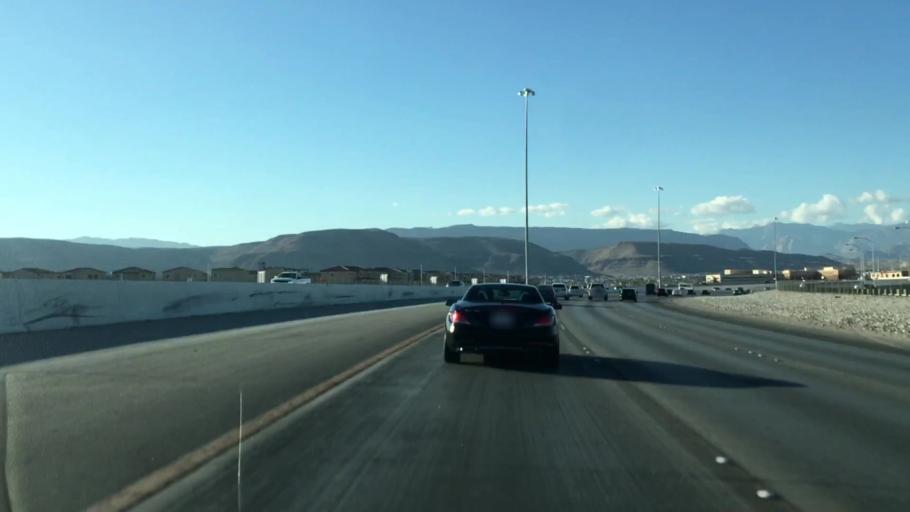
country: US
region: Nevada
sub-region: Clark County
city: Spring Valley
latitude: 36.0666
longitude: -115.2833
